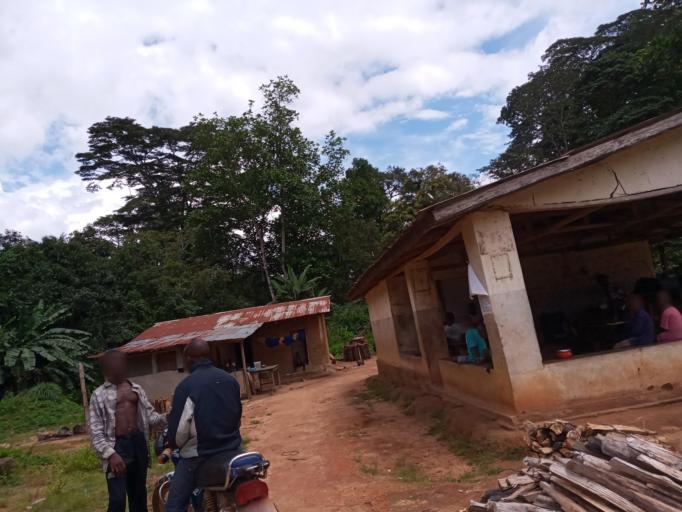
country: SL
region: Eastern Province
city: Koidu
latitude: 8.6213
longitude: -10.8606
